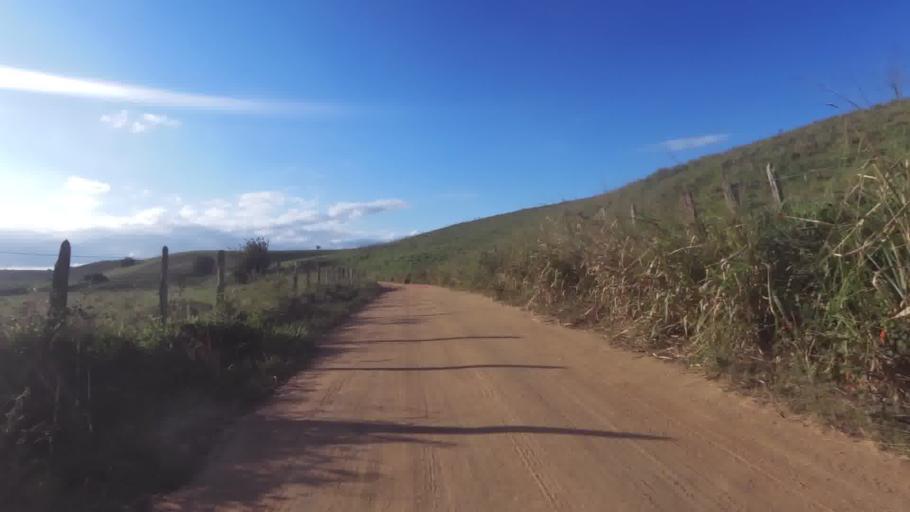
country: BR
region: Espirito Santo
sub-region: Marataizes
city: Marataizes
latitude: -21.1362
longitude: -41.0179
